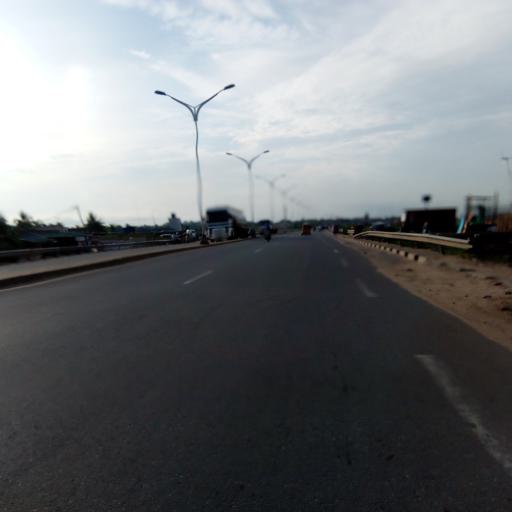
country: TG
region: Maritime
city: Lome
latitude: 6.1882
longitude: 1.2758
